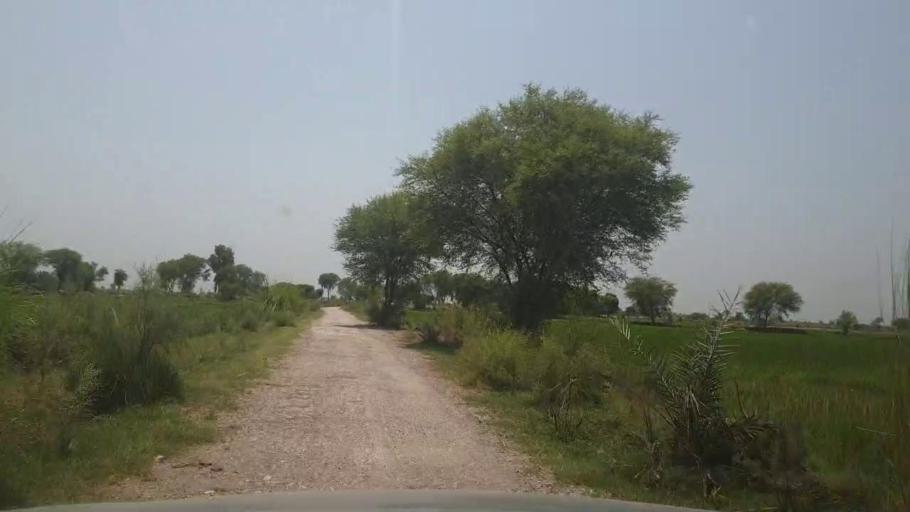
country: PK
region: Sindh
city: Lakhi
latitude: 27.8478
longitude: 68.6645
